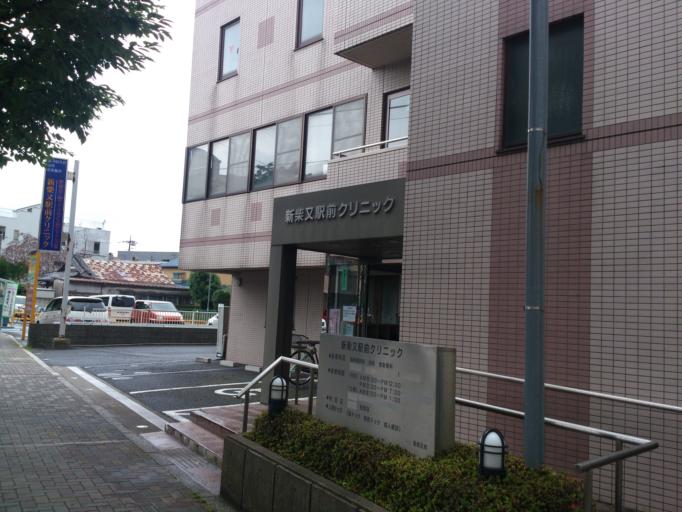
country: JP
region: Chiba
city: Matsudo
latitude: 35.7502
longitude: 139.8783
